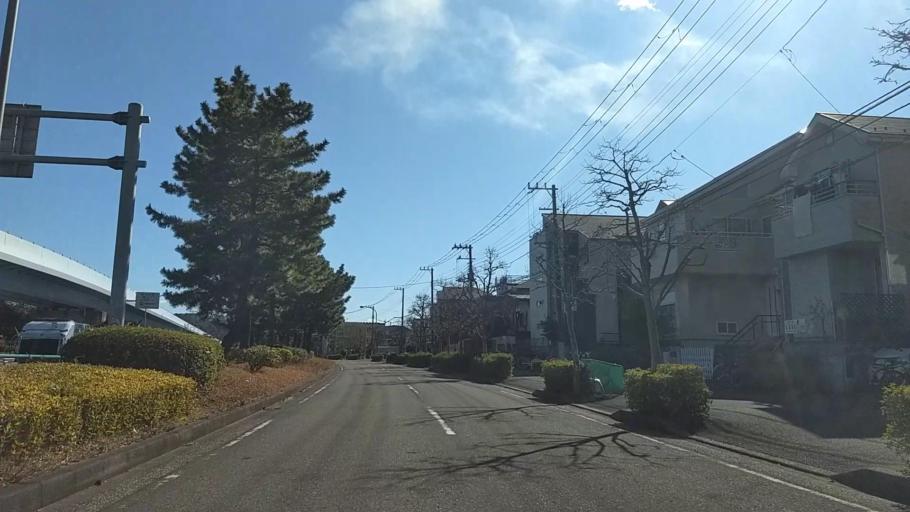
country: JP
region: Kanagawa
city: Yokosuka
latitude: 35.3367
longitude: 139.6317
